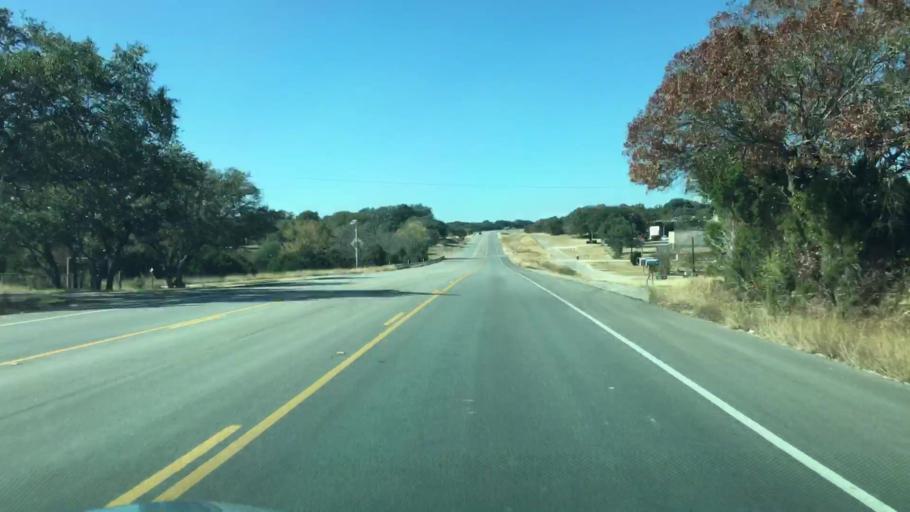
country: US
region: Texas
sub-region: Hays County
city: Dripping Springs
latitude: 30.2078
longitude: -98.1480
